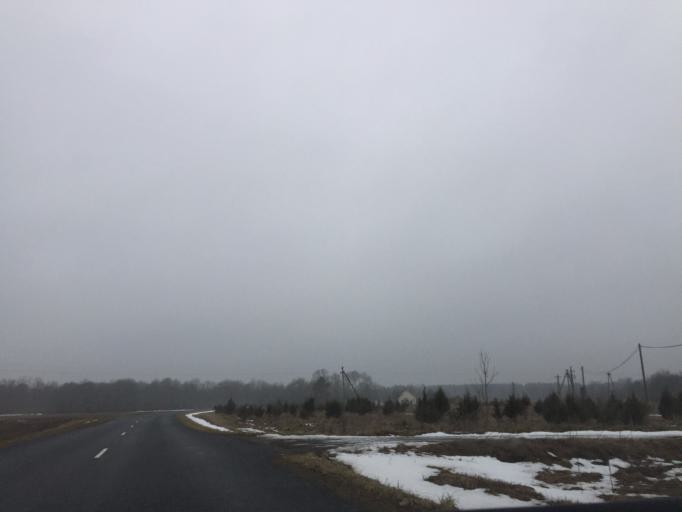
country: EE
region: Saare
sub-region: Orissaare vald
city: Orissaare
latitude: 58.3921
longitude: 22.8401
